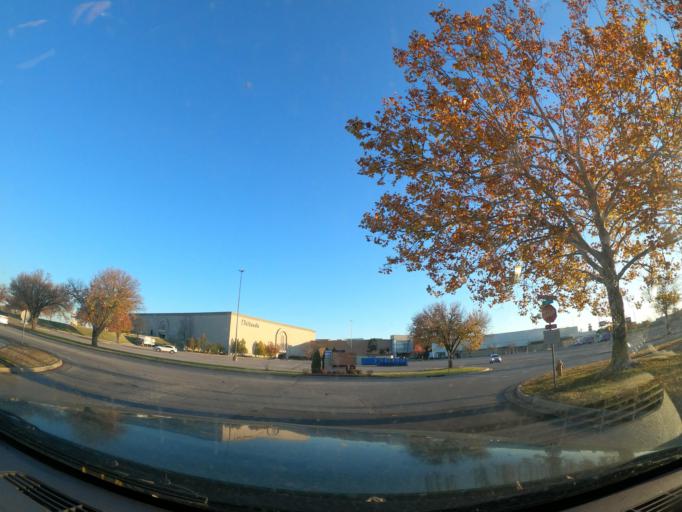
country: US
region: Oklahoma
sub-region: Tulsa County
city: Broken Arrow
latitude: 36.0652
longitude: -95.8836
